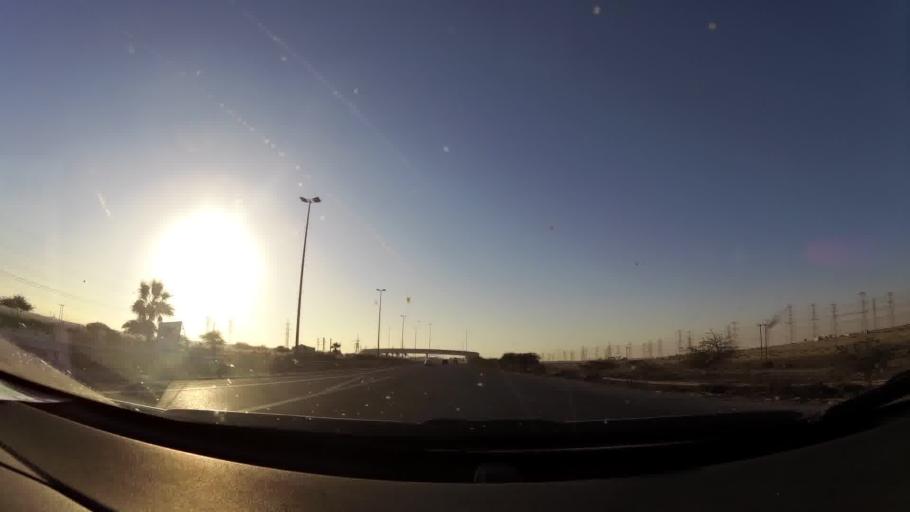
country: KW
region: Al Ahmadi
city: Al Fahahil
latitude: 28.8888
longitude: 48.2247
